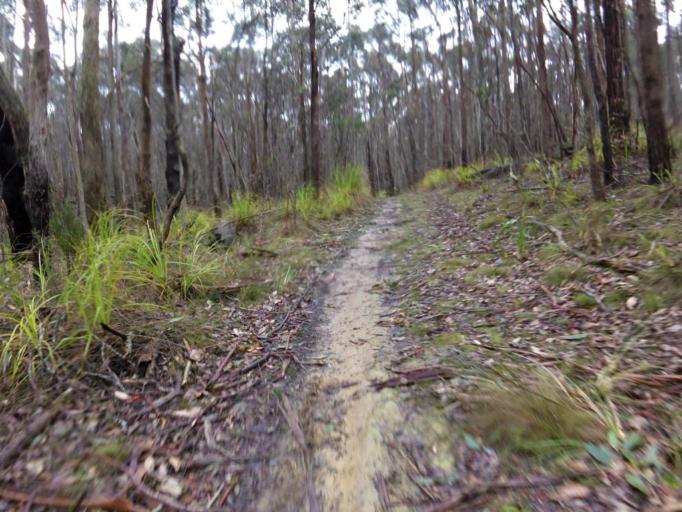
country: AU
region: Victoria
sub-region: Moorabool
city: Bacchus Marsh
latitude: -37.4180
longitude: 144.4875
